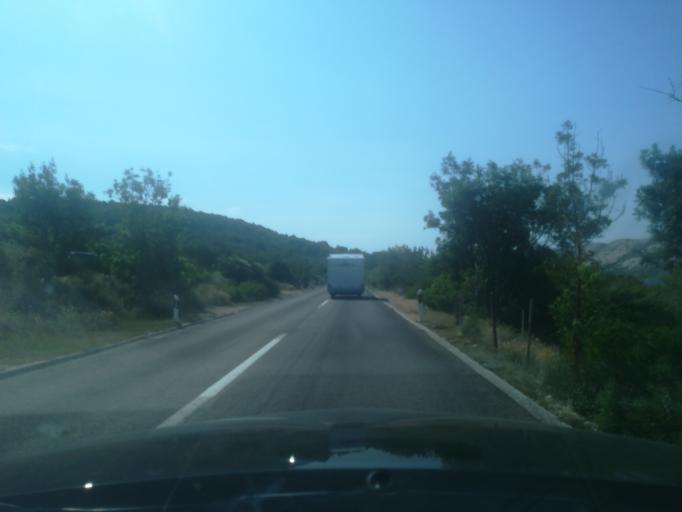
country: HR
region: Primorsko-Goranska
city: Banjol
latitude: 44.7203
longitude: 14.8234
